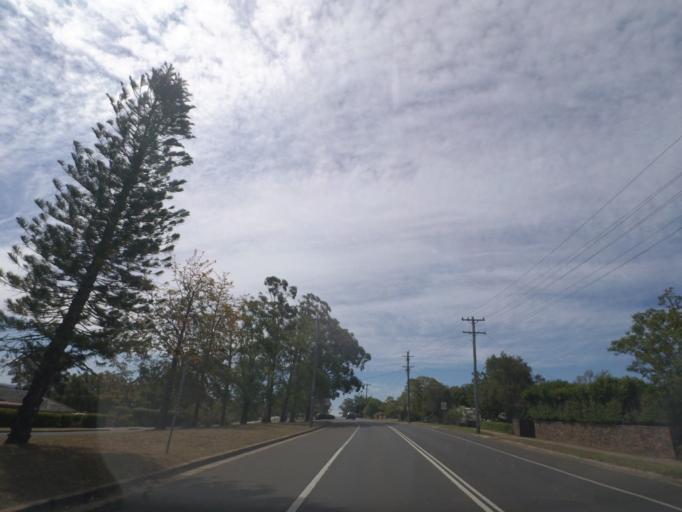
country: AU
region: New South Wales
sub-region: Camden
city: Camden South
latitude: -34.0674
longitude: 150.6940
